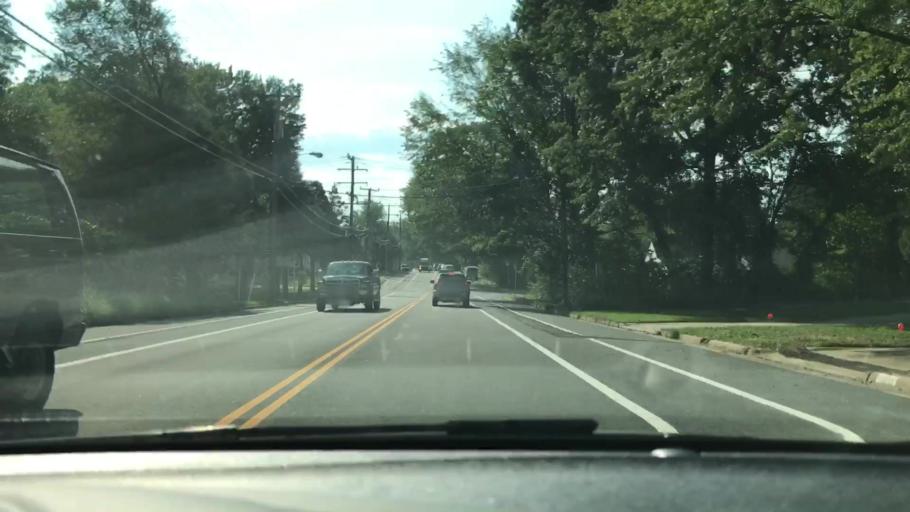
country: US
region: Virginia
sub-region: Fairfax County
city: Jefferson
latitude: 38.8572
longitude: -77.1841
